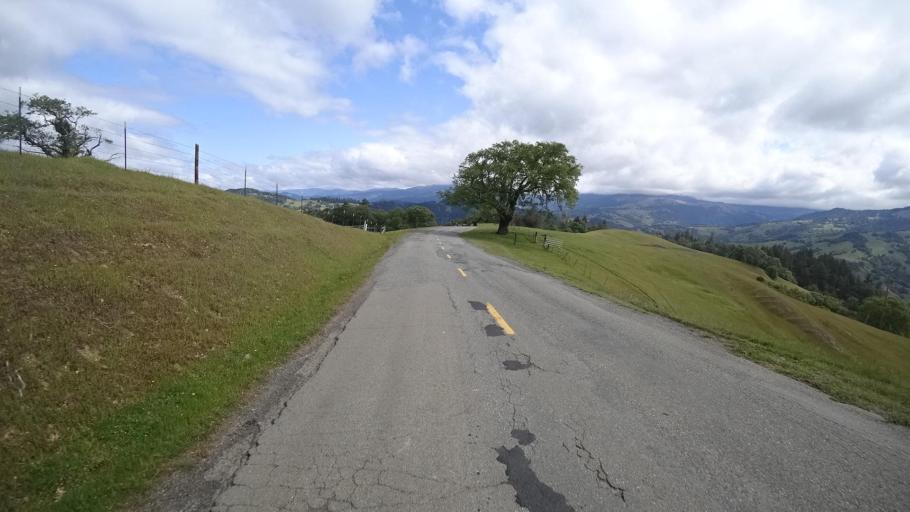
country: US
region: California
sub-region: Humboldt County
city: Redway
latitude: 40.1559
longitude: -123.6221
